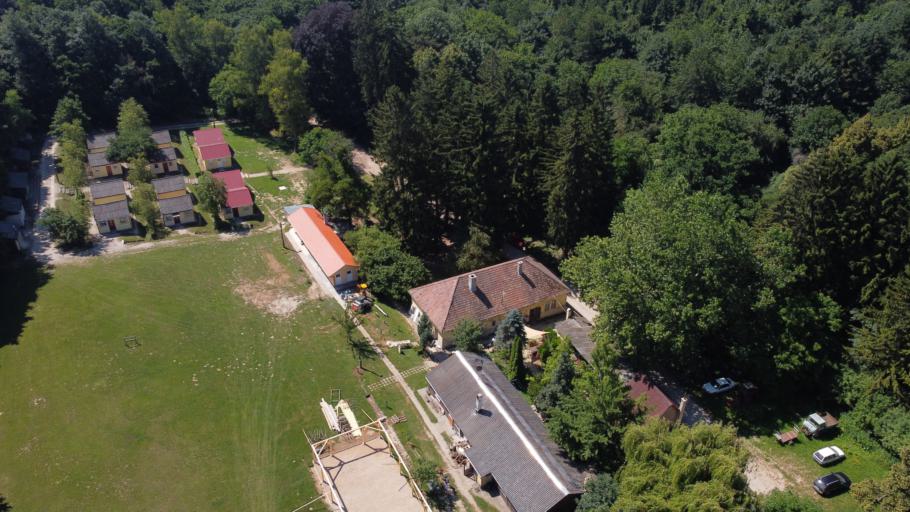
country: HU
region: Komarom-Esztergom
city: Labatlan
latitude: 47.6881
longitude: 18.5205
